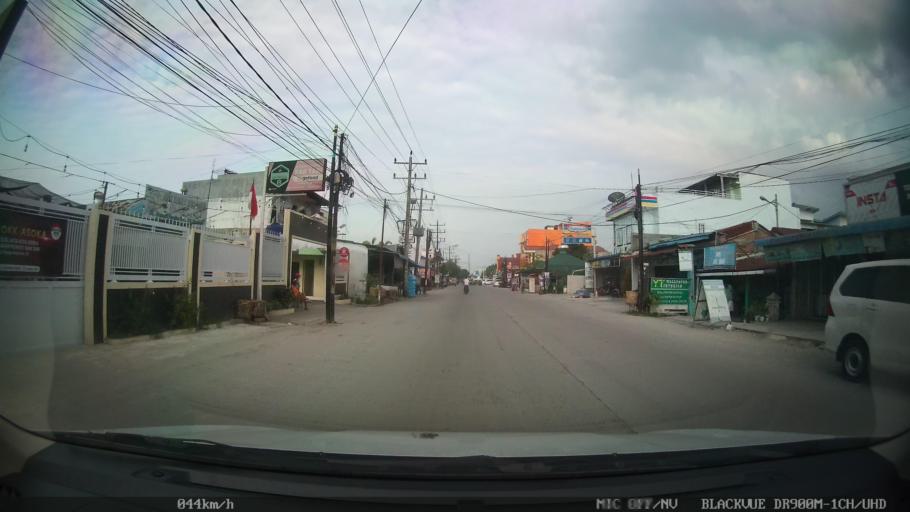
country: ID
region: North Sumatra
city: Sunggal
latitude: 3.5638
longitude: 98.6211
